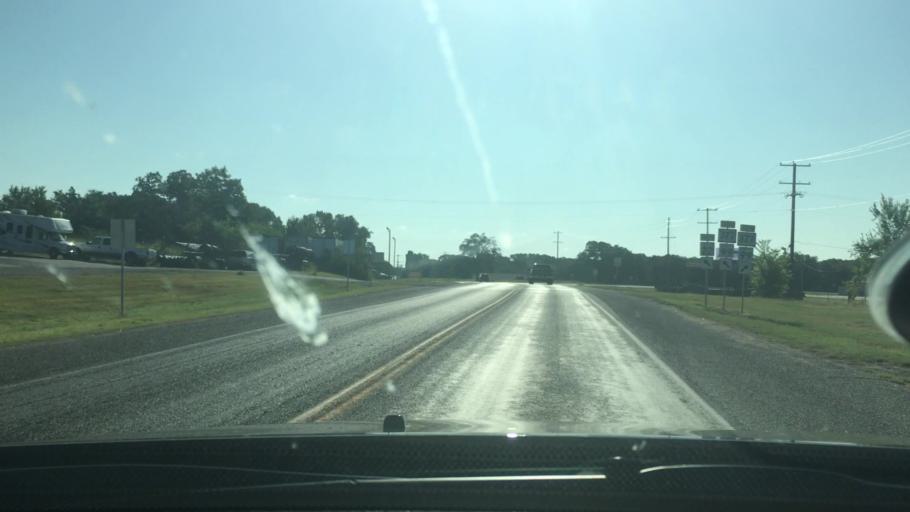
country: US
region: Oklahoma
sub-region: Johnston County
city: Tishomingo
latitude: 34.2371
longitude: -96.7016
